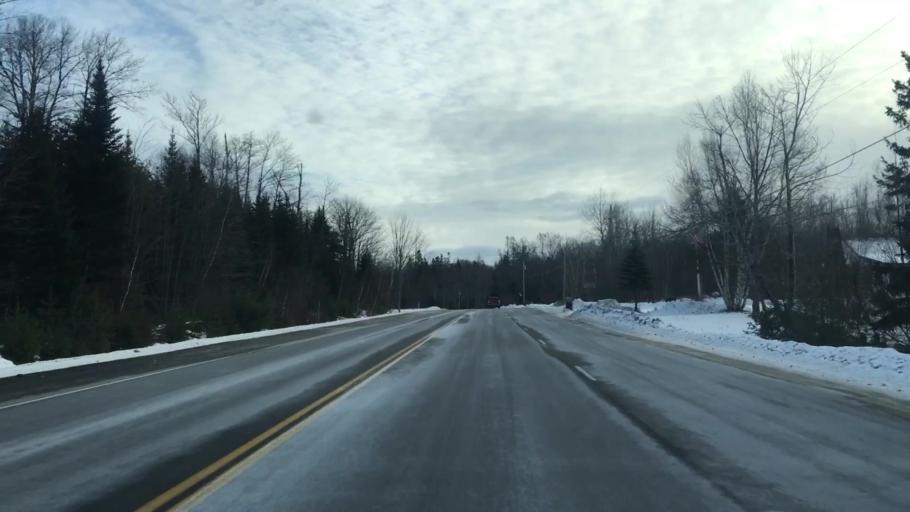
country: US
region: Maine
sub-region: Washington County
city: Machias
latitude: 44.9503
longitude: -67.6731
